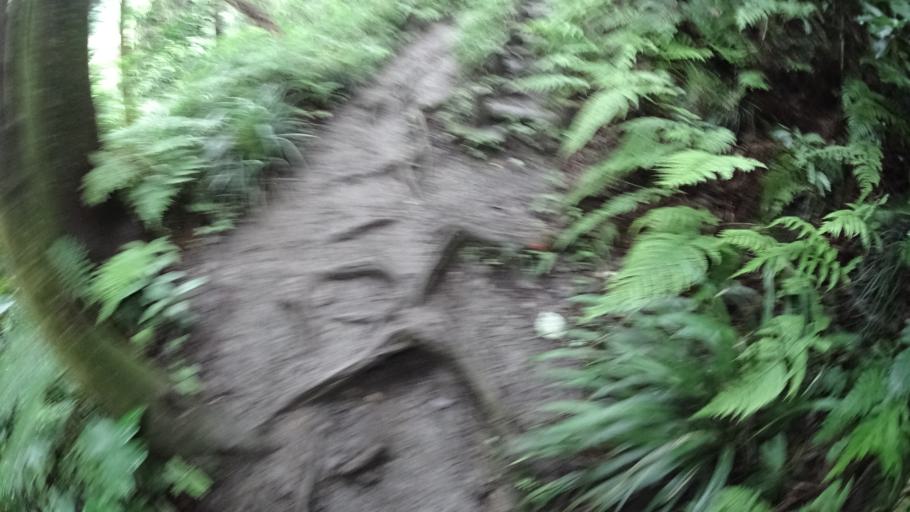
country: JP
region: Kanagawa
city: Yokosuka
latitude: 35.2537
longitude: 139.6339
